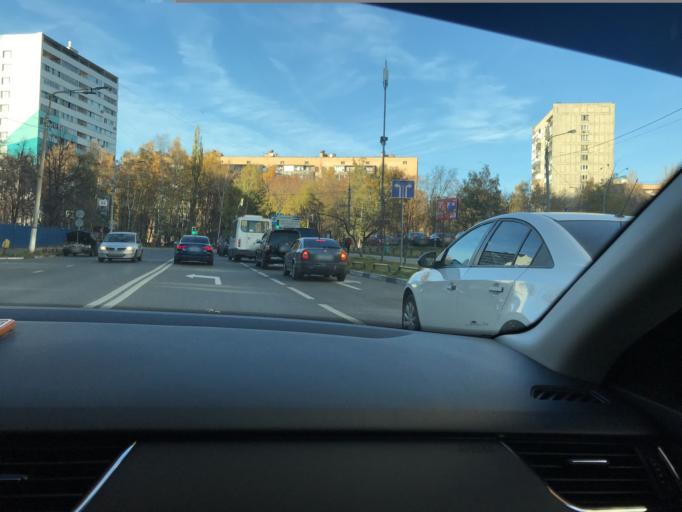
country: RU
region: Moscow
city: Khimki
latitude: 55.8863
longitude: 37.4264
